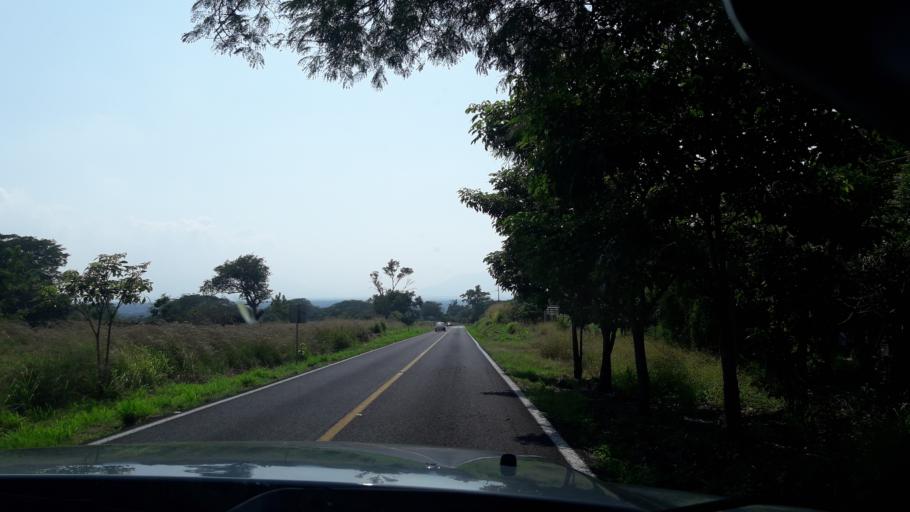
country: MX
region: Colima
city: Comala
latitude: 19.3413
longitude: -103.7432
